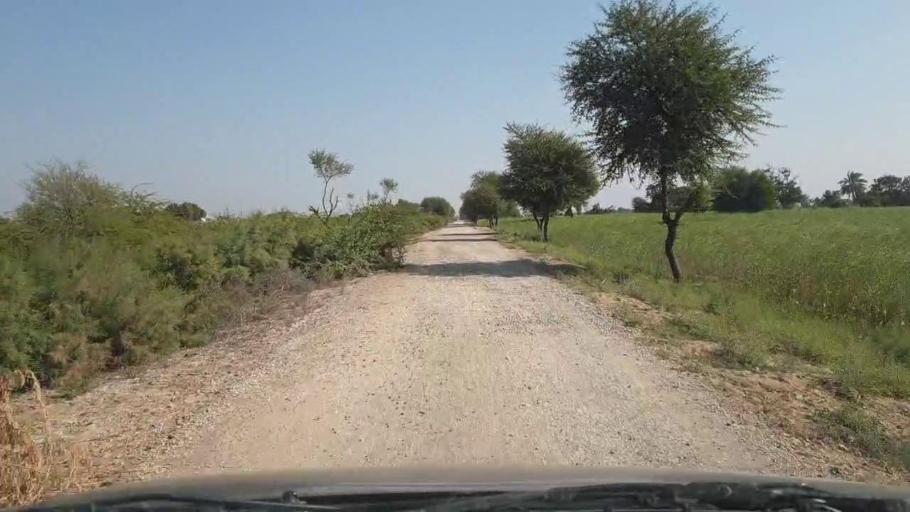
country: PK
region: Sindh
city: Samaro
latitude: 25.2038
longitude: 69.2805
